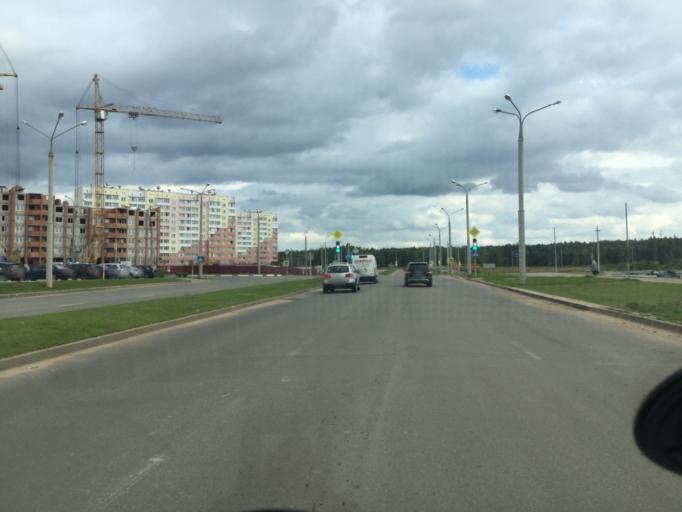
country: BY
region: Vitebsk
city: Vitebsk
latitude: 55.1639
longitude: 30.2746
